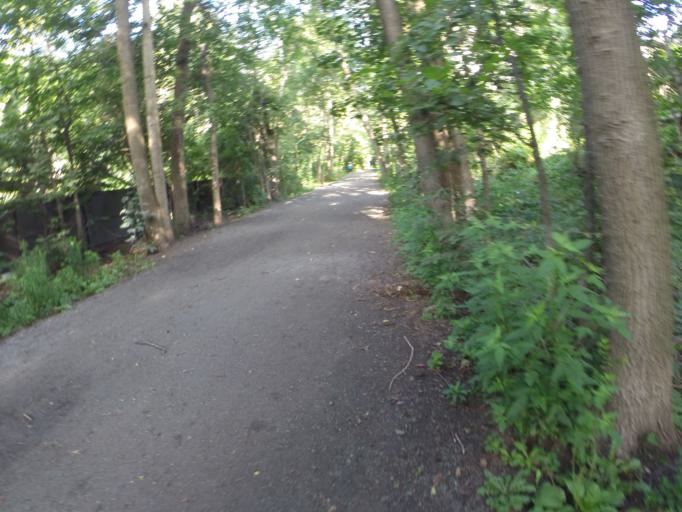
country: CA
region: Ontario
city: Toronto
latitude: 43.7017
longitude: -79.4162
